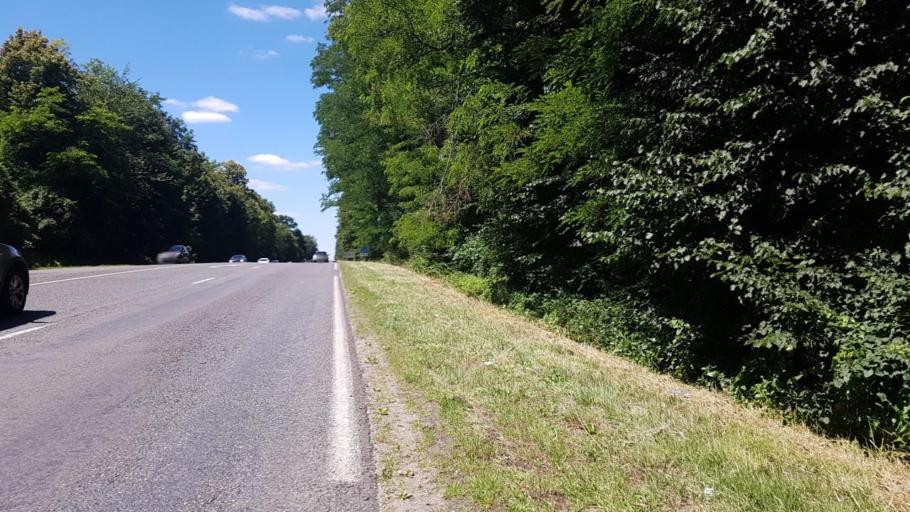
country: FR
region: Ile-de-France
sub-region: Departement de Seine-et-Marne
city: Saint-Jean-les-Deux-Jumeaux
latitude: 48.9591
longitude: 2.9923
